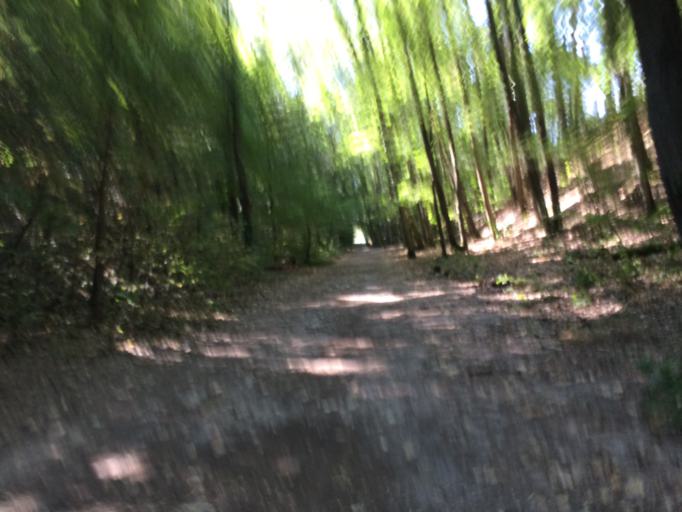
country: FR
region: Ile-de-France
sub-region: Departement de l'Essonne
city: Les Ulis
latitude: 48.6820
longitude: 2.1544
